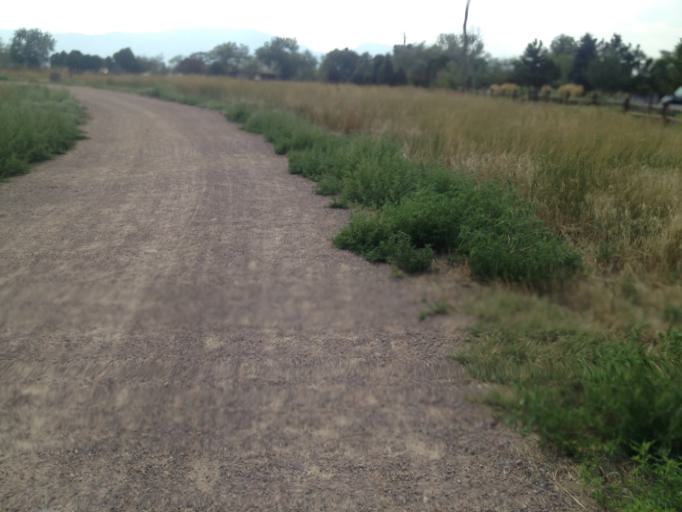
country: US
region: Colorado
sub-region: Boulder County
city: Superior
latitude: 39.9723
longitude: -105.1818
